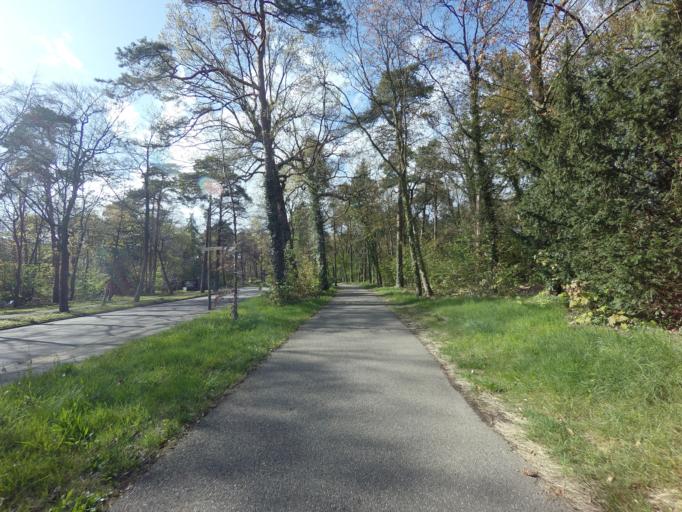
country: NL
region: Utrecht
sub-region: Gemeente Zeist
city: Zeist
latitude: 52.0775
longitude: 5.2526
